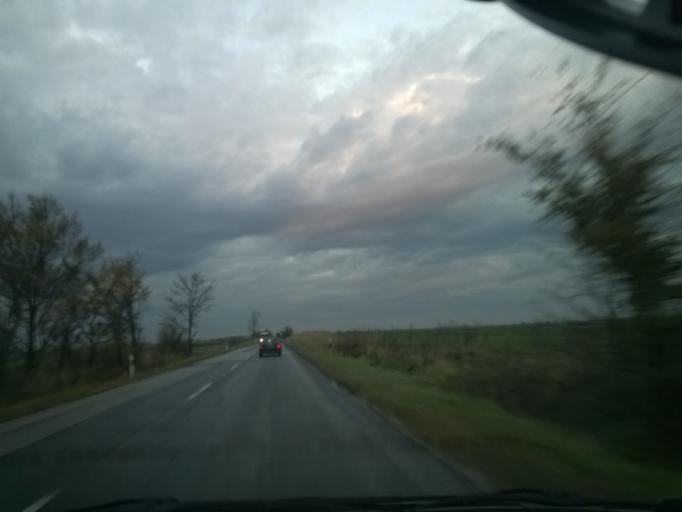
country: HU
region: Bacs-Kiskun
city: Tass
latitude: 47.0465
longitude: 19.0230
